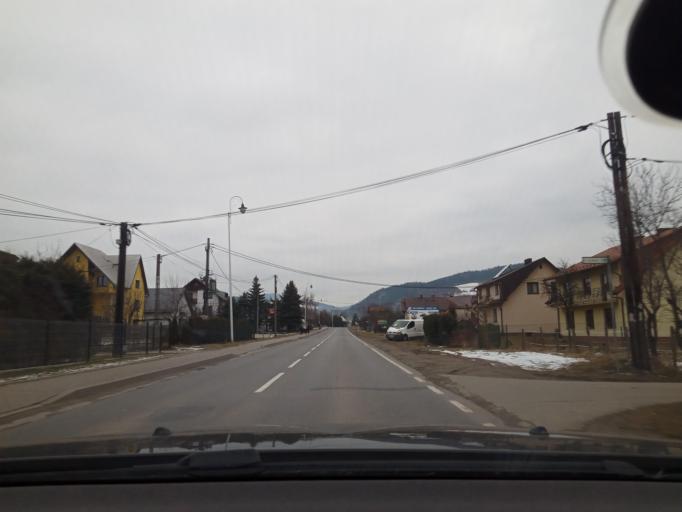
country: PL
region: Lesser Poland Voivodeship
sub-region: Powiat limanowski
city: Kamienica
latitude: 49.5697
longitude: 20.3534
